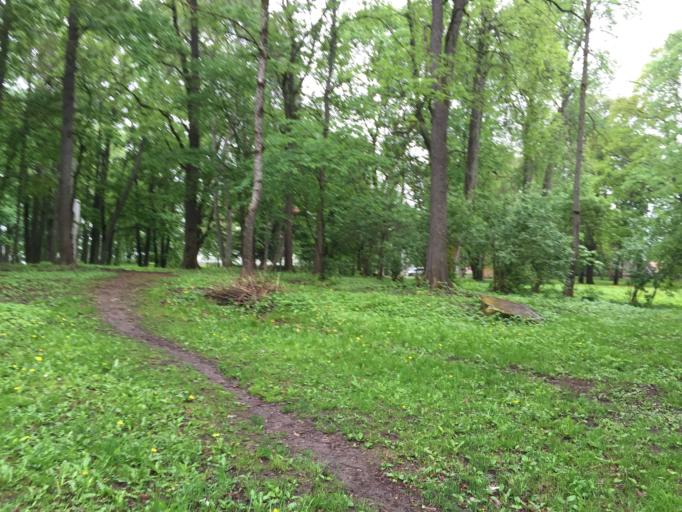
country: LV
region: Lielvarde
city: Lielvarde
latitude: 56.7125
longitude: 24.8363
